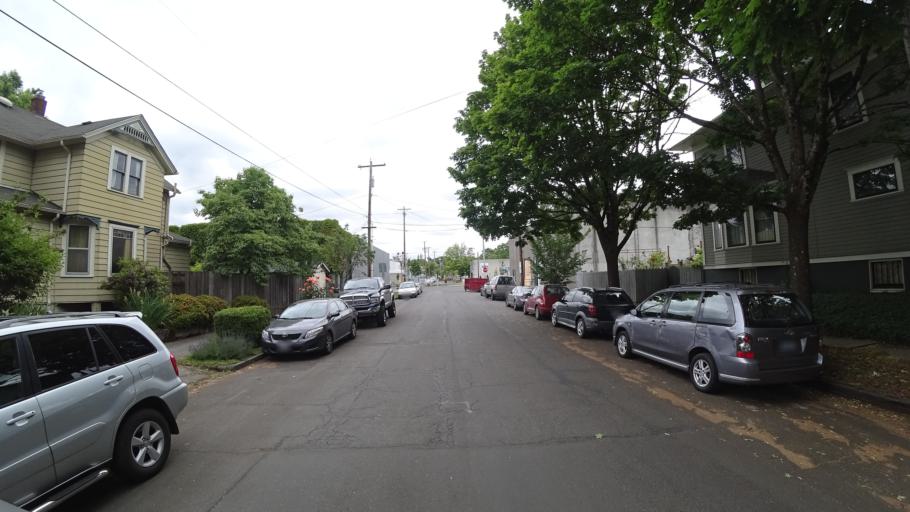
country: US
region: Oregon
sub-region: Multnomah County
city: Portland
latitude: 45.4982
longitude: -122.6491
